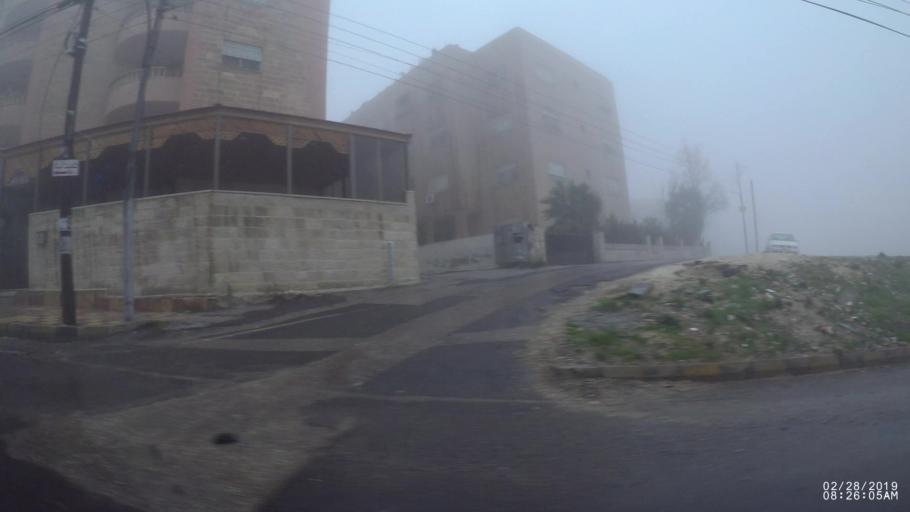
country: JO
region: Amman
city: Al Jubayhah
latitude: 32.0056
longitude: 35.8832
